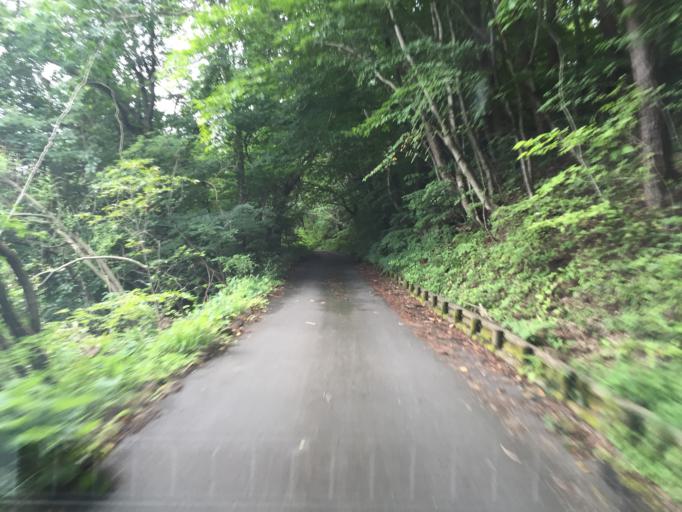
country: JP
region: Fukushima
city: Motomiya
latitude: 37.5641
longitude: 140.3024
